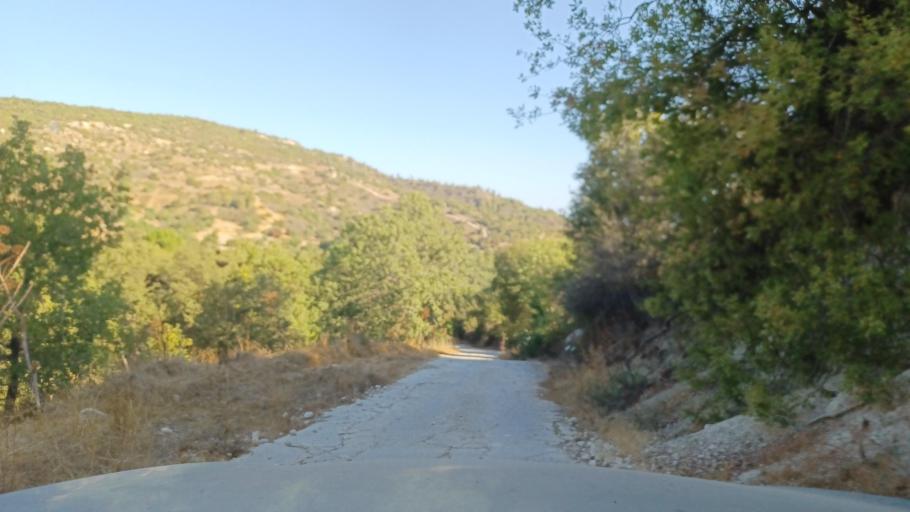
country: CY
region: Pafos
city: Polis
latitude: 34.9957
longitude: 32.4909
